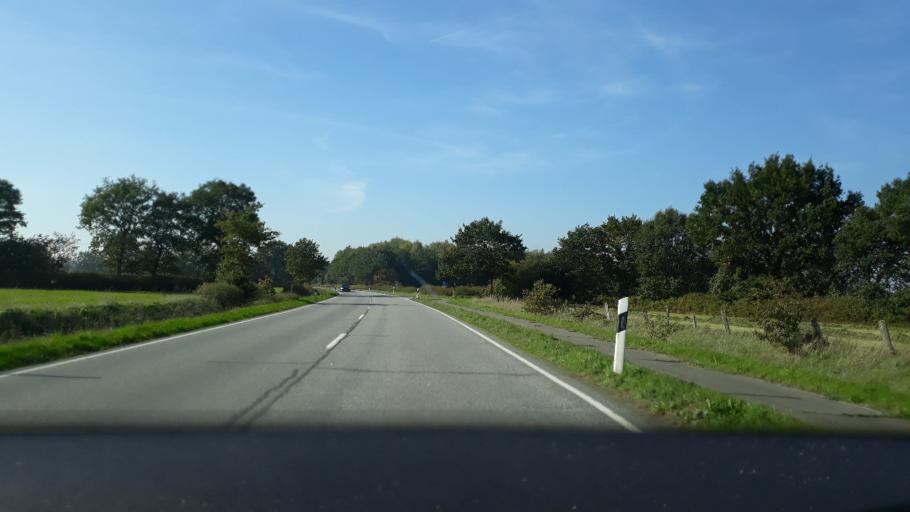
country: DE
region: Schleswig-Holstein
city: Klein Bennebek
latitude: 54.4041
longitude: 9.4767
